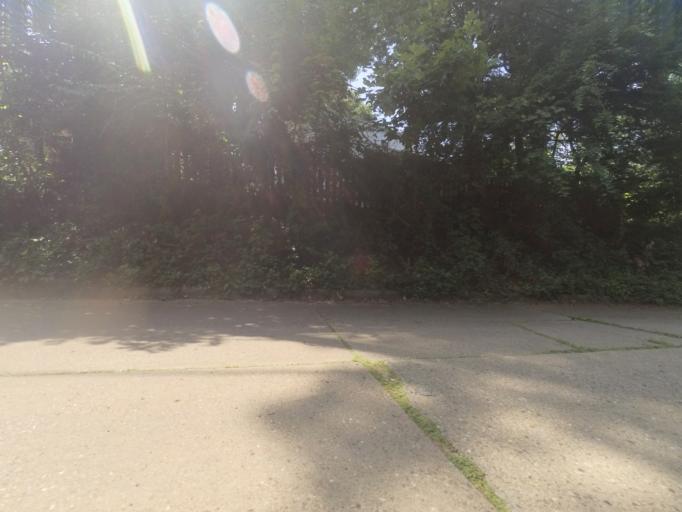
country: US
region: West Virginia
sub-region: Cabell County
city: Huntington
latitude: 38.4062
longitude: -82.4174
